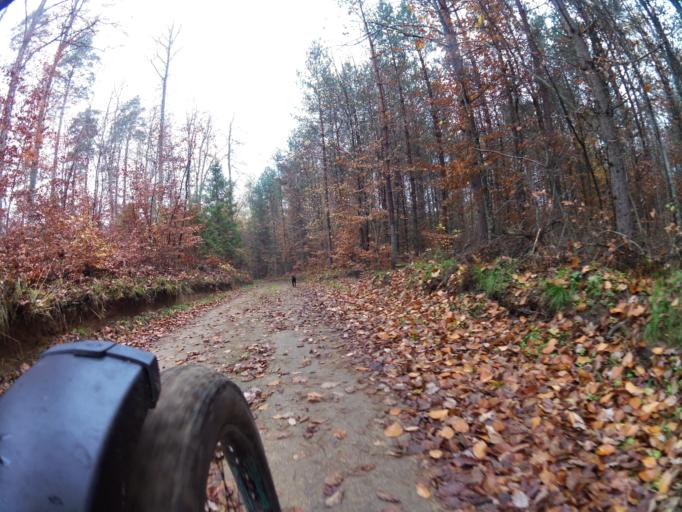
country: PL
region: Pomeranian Voivodeship
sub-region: Powiat wejherowski
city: Orle
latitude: 54.6982
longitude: 18.1559
